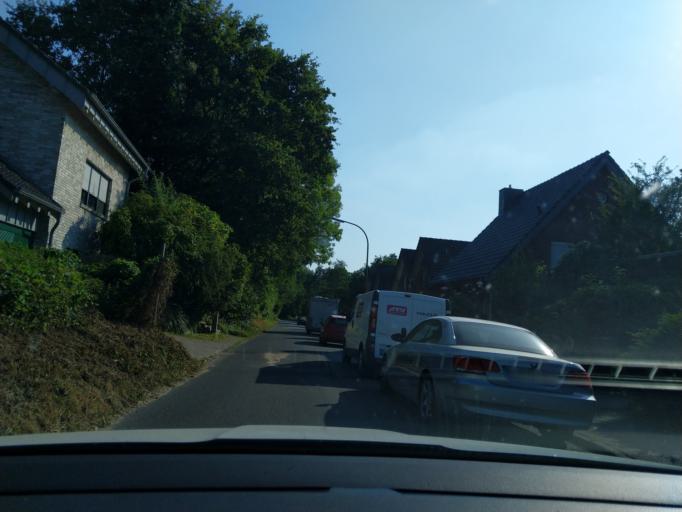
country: DE
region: North Rhine-Westphalia
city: Wegberg
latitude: 51.1317
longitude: 6.2701
